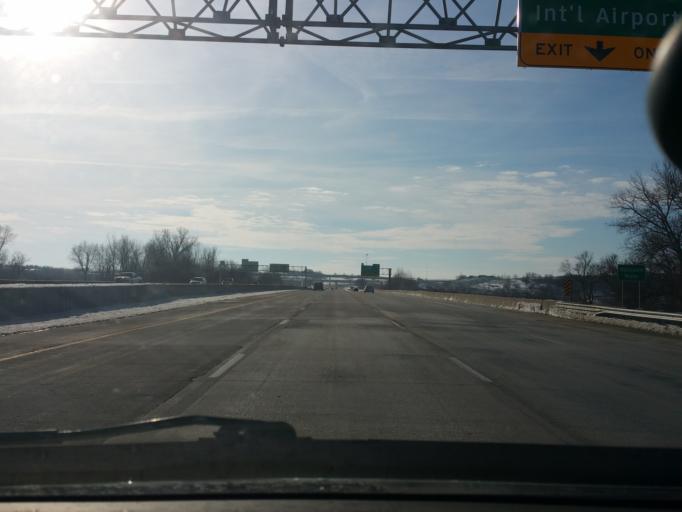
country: US
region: Iowa
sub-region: Polk County
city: West Des Moines
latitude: 41.5344
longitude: -93.7744
